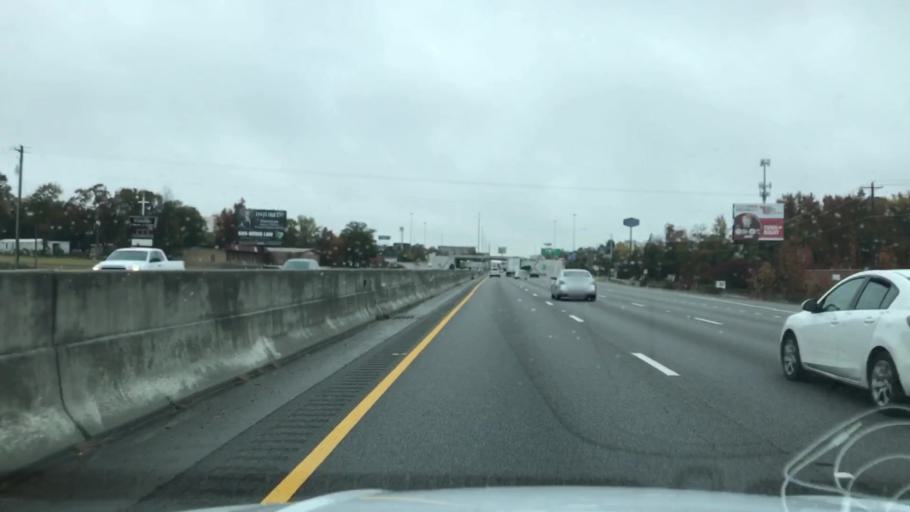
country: US
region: South Carolina
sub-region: Lexington County
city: West Columbia
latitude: 33.9983
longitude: -81.1088
